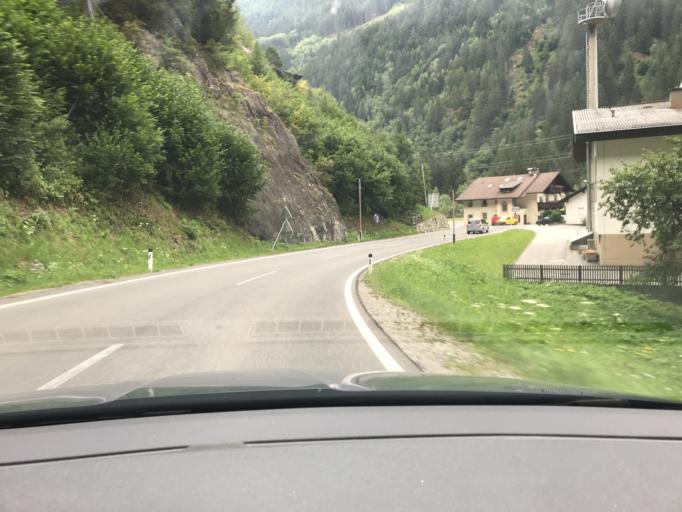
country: AT
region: Tyrol
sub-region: Politischer Bezirk Lienz
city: Hopfgarten in Defereggen
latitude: 46.9359
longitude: 12.5716
